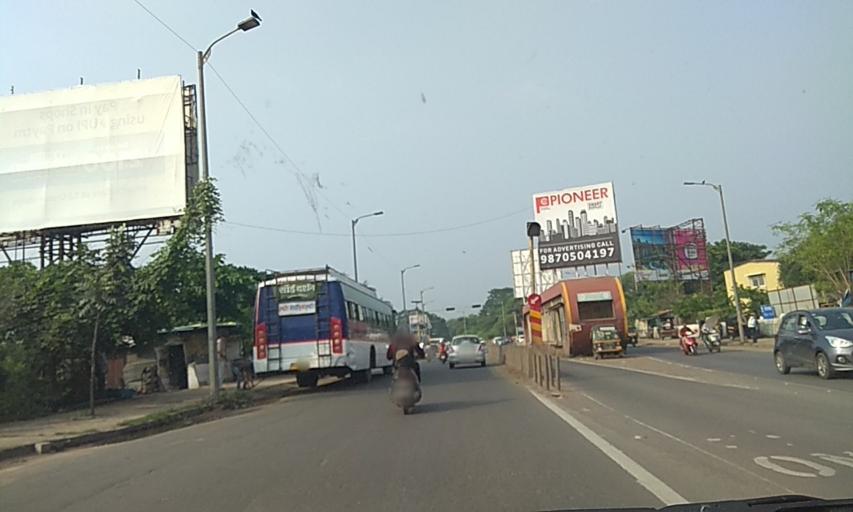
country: IN
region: Maharashtra
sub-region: Pune Division
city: Shivaji Nagar
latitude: 18.5377
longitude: 73.8638
